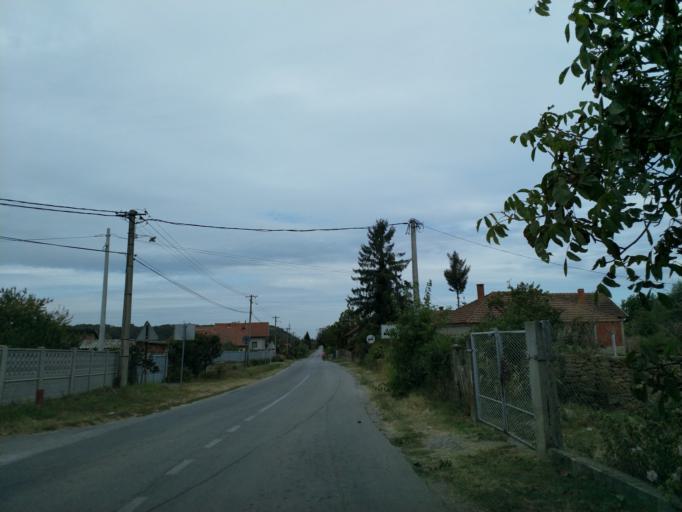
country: RS
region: Central Serbia
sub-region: Pomoravski Okrug
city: Cuprija
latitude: 43.9365
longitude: 21.3210
